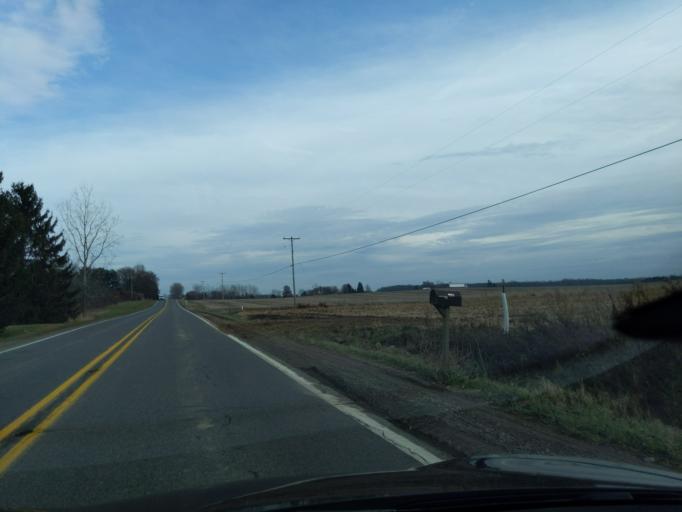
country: US
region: Michigan
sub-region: Ingham County
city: Mason
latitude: 42.6400
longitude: -84.3944
